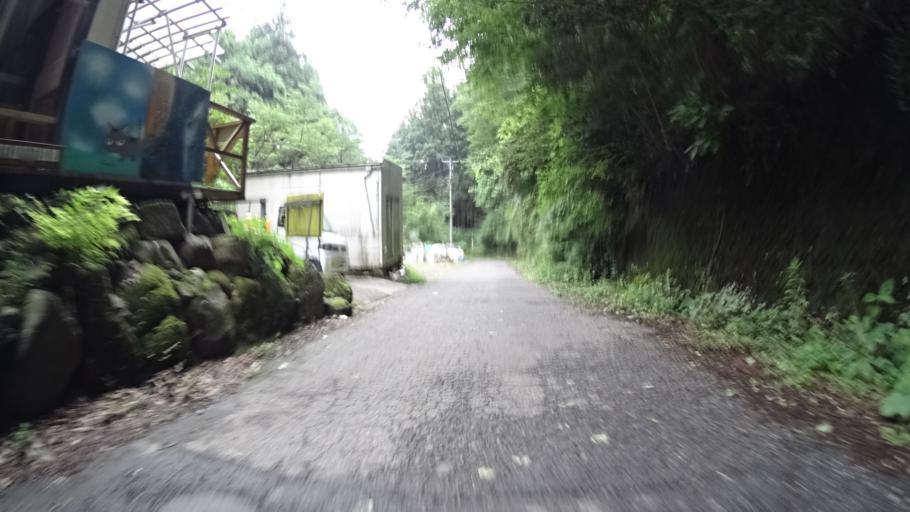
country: JP
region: Kanagawa
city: Atsugi
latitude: 35.4989
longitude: 139.2660
